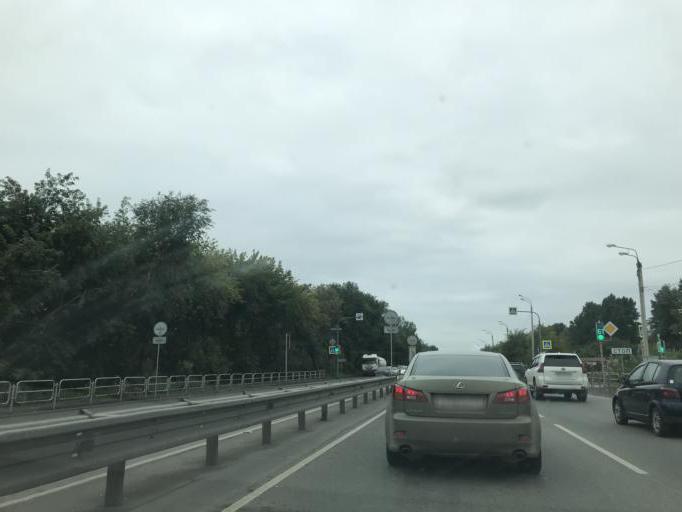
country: RU
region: Chelyabinsk
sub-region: Gorod Chelyabinsk
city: Chelyabinsk
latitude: 55.1792
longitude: 61.4203
